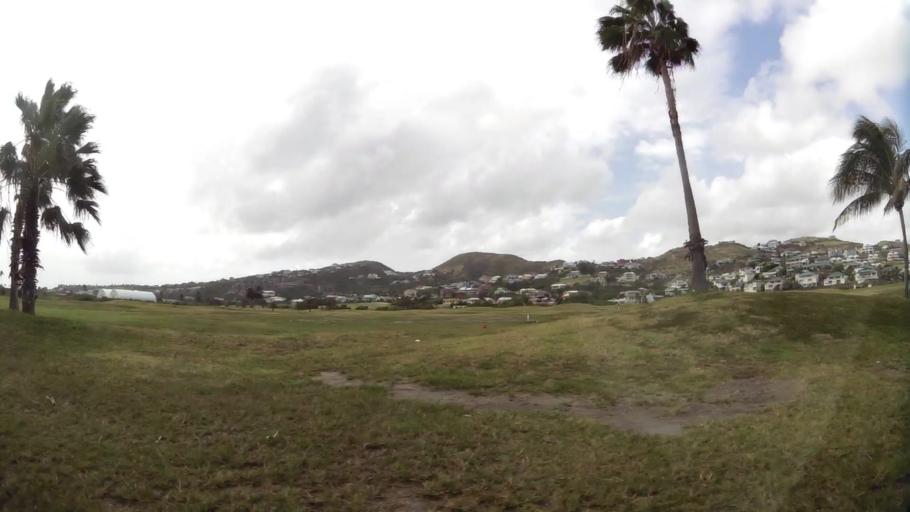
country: KN
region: Saint Peter Basseterre
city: Monkey Hill
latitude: 17.2954
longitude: -62.6869
